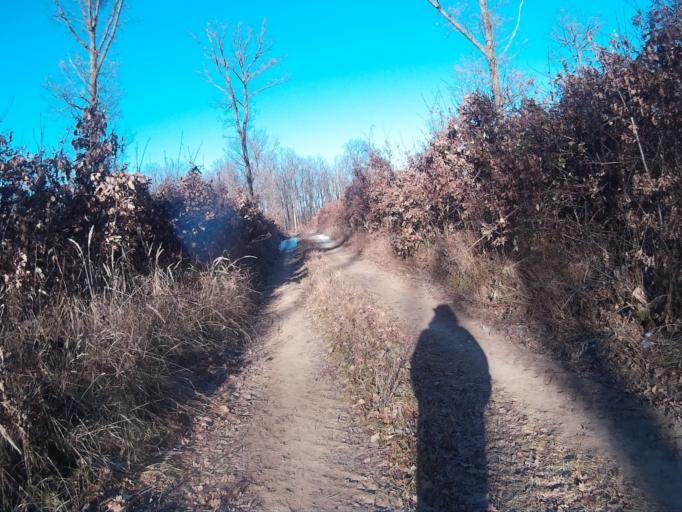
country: HU
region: Borsod-Abauj-Zemplen
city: Putnok
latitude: 48.4112
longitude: 20.4817
